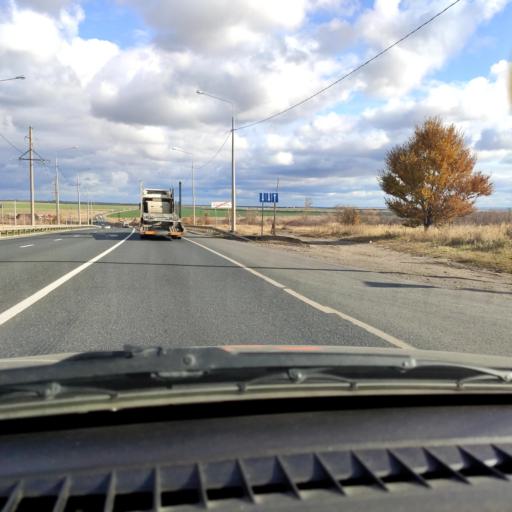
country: RU
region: Samara
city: Varlamovo
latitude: 53.1981
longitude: 48.3727
